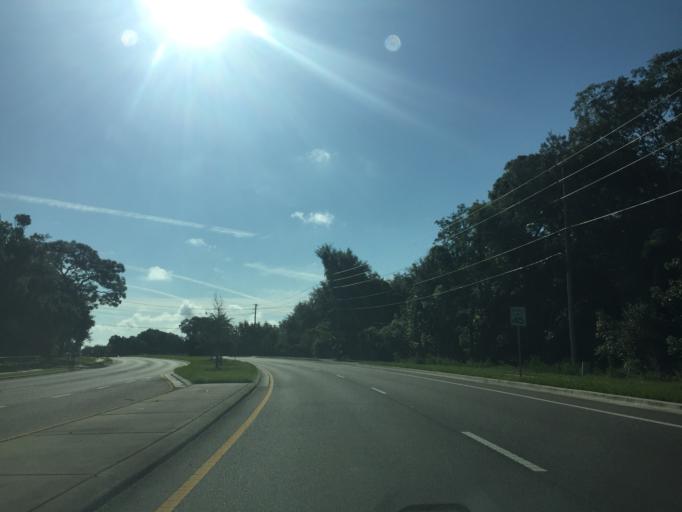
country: US
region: Florida
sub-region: Seminole County
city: Winter Springs
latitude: 28.6710
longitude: -81.2985
